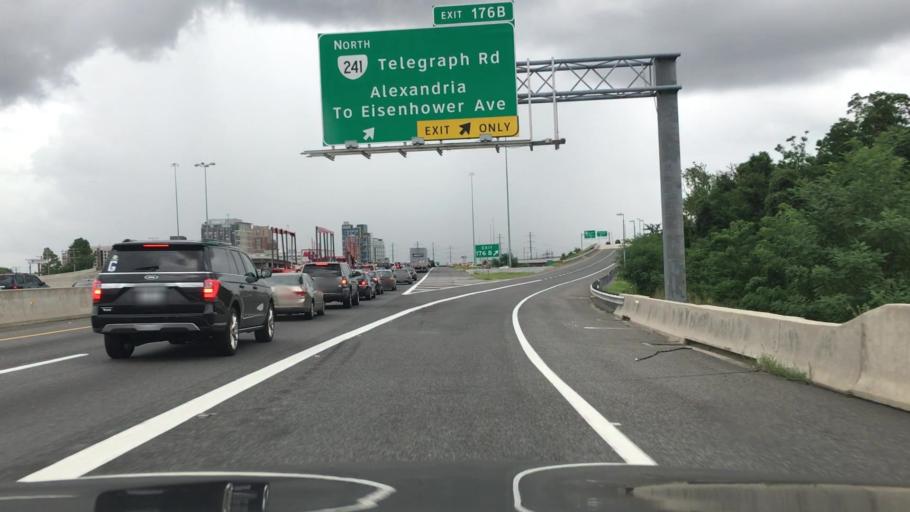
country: US
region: Virginia
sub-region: Fairfax County
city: Huntington
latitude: 38.8008
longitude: -77.0832
